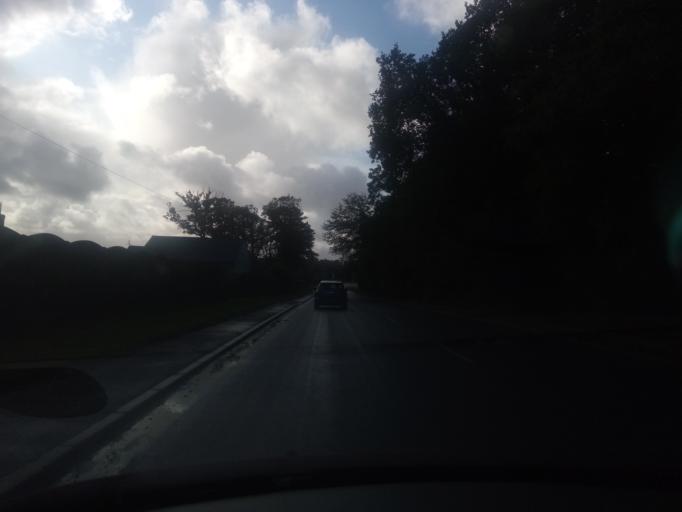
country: GB
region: England
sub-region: Cumbria
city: Carlisle
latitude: 54.9353
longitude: -2.9452
